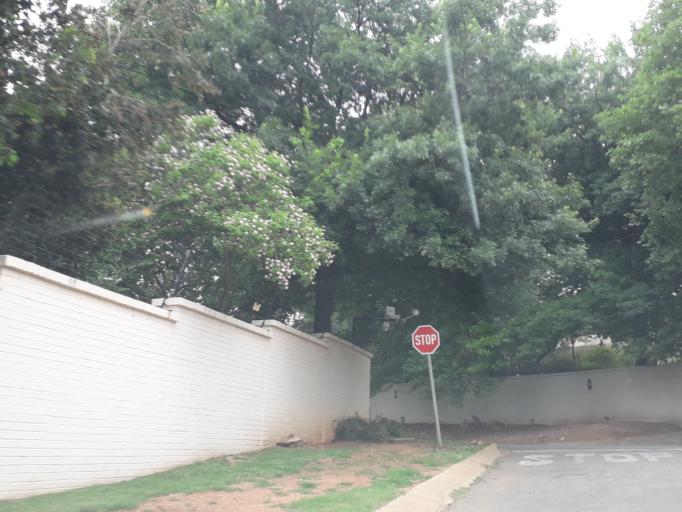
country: ZA
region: Gauteng
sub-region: City of Johannesburg Metropolitan Municipality
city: Midrand
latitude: -26.0447
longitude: 28.0372
